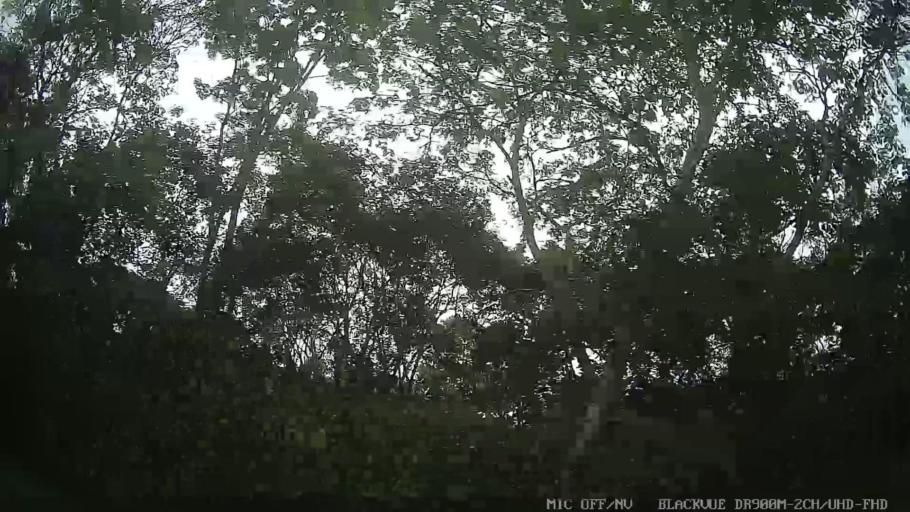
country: BR
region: Sao Paulo
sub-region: Santa Branca
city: Santa Branca
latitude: -23.5325
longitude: -45.7410
